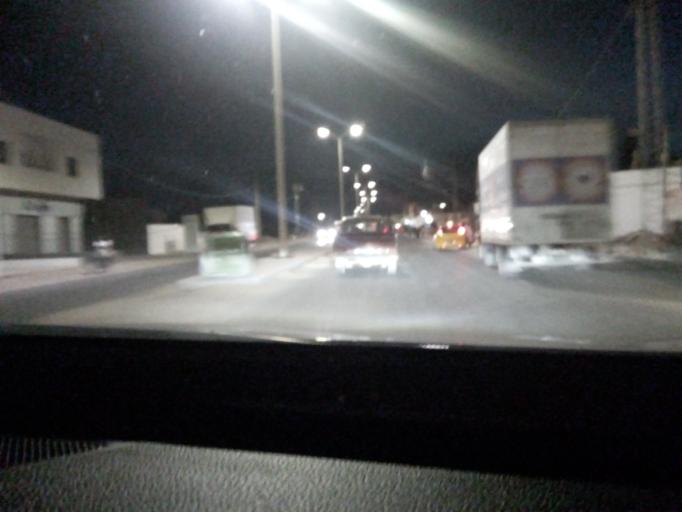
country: TN
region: Safaqis
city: Sfax
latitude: 34.7312
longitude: 10.6695
